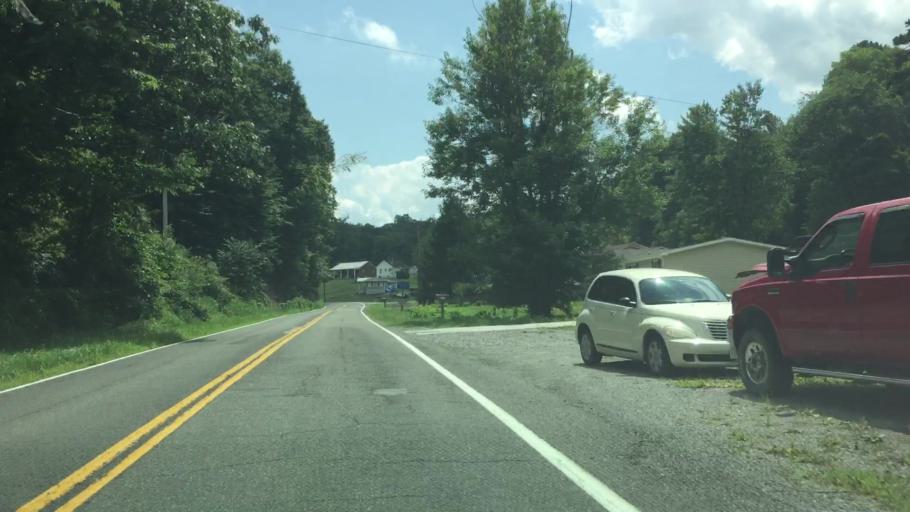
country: US
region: Virginia
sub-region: Pulaski County
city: Pulaski
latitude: 37.0338
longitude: -80.7248
